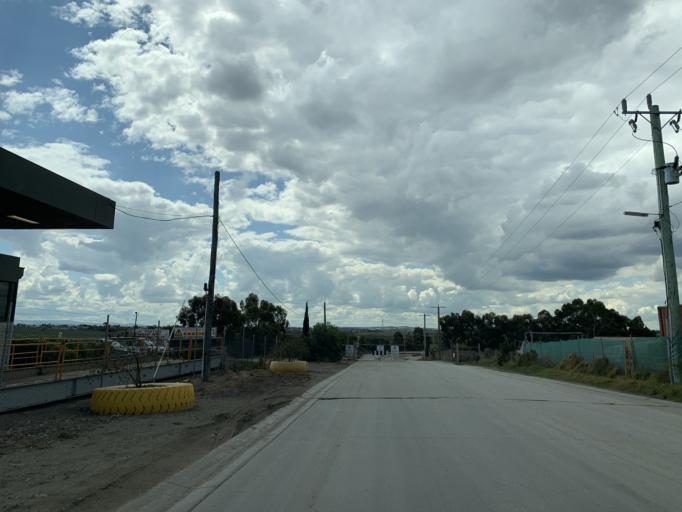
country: AU
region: Victoria
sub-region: Brimbank
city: Kealba
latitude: -37.7468
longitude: 144.8342
